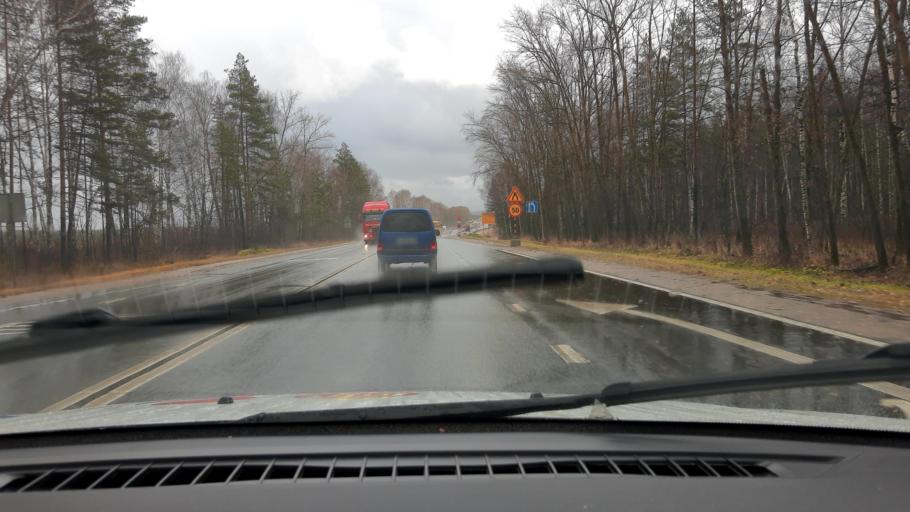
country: RU
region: Nizjnij Novgorod
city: Pamyat' Parizhskoy Kommuny
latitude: 56.0295
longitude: 44.5447
